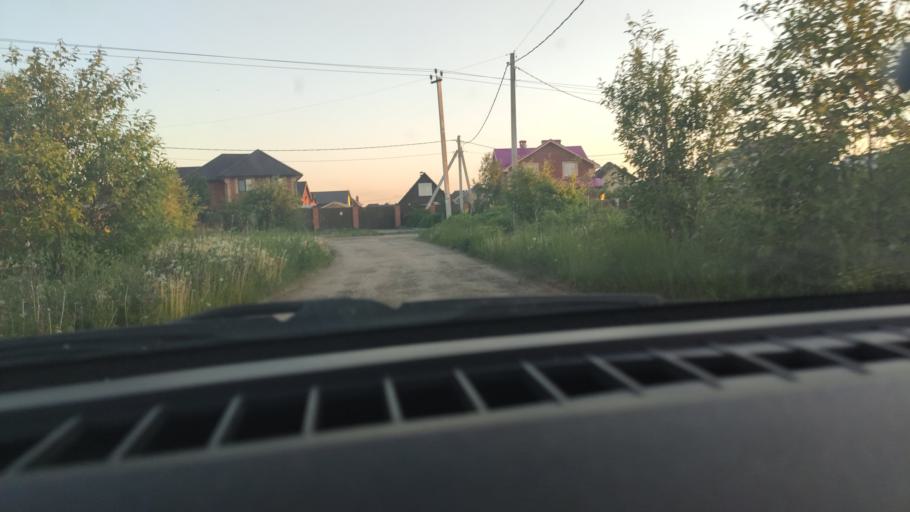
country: RU
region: Perm
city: Kultayevo
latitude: 57.9024
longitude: 55.9726
